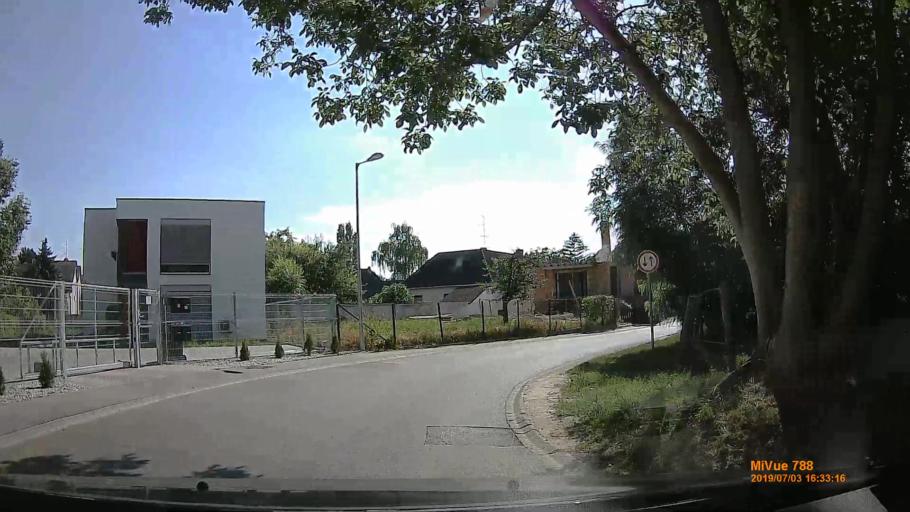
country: HU
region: Gyor-Moson-Sopron
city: Gyor
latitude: 47.7038
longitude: 17.6355
